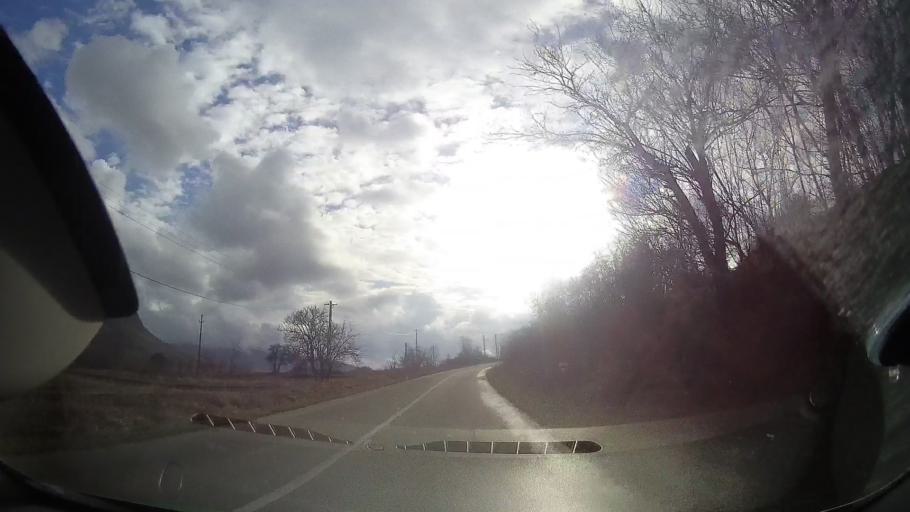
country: RO
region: Alba
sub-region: Comuna Rimetea
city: Rimetea
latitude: 46.4468
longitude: 23.5655
